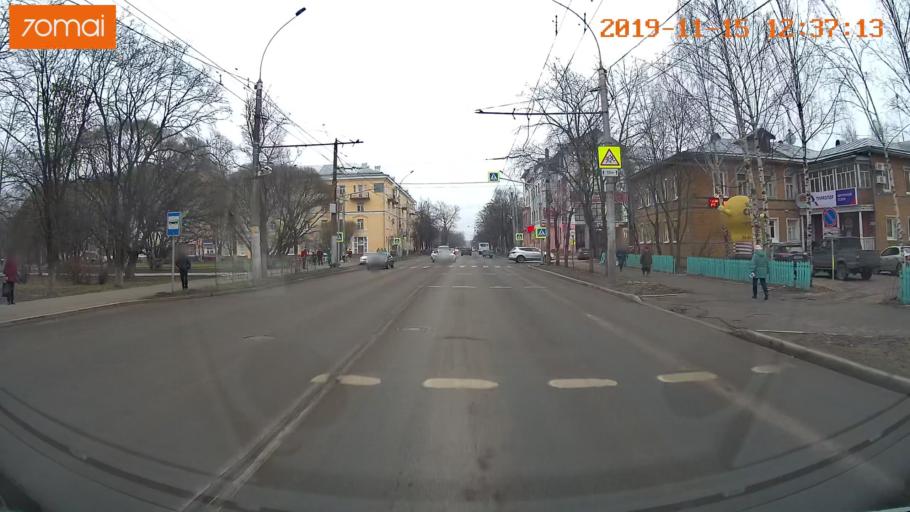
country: RU
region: Vologda
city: Vologda
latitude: 59.2106
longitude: 39.8964
